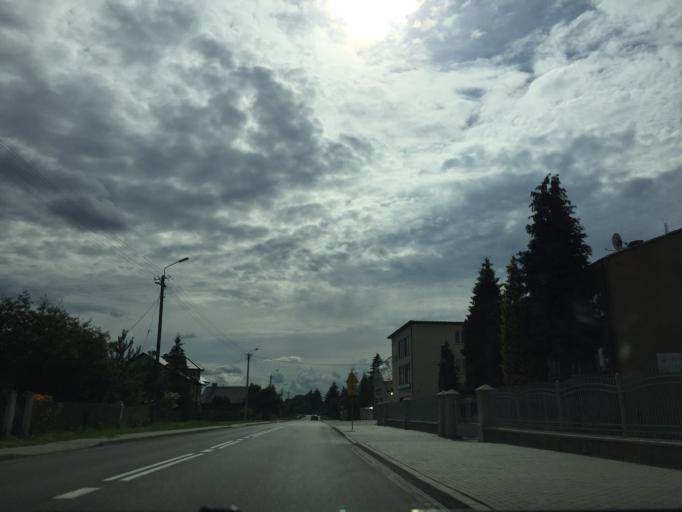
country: PL
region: Lublin Voivodeship
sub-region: Powiat lukowski
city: Trzebieszow
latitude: 51.9870
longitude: 22.5439
